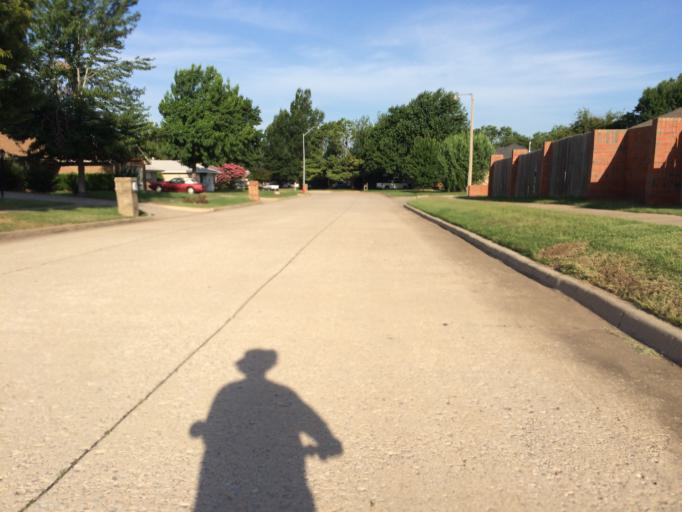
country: US
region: Oklahoma
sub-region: Cleveland County
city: Norman
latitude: 35.2244
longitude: -97.4914
